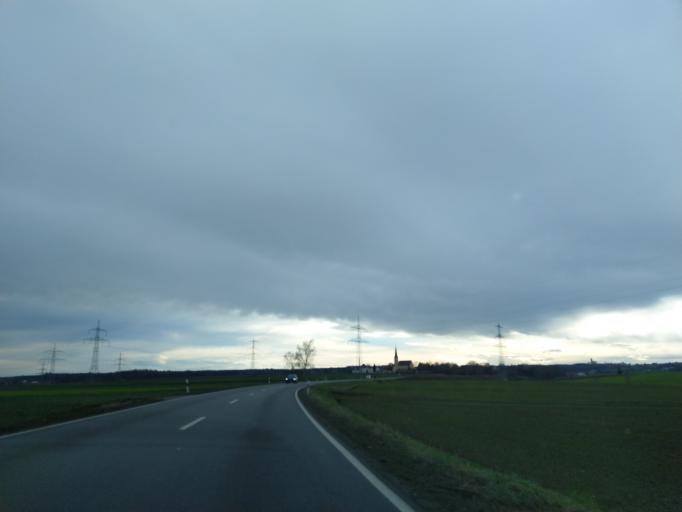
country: DE
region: Bavaria
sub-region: Lower Bavaria
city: Kunzing
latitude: 48.6599
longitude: 13.0452
